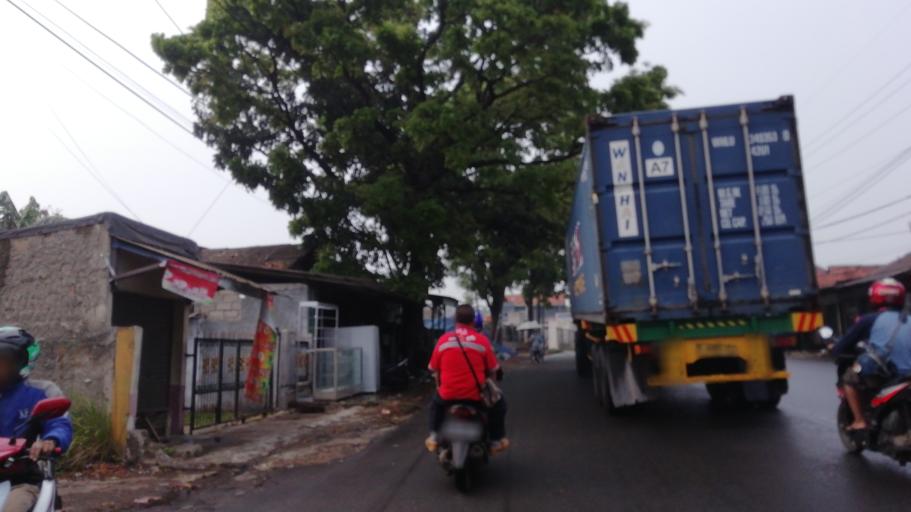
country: ID
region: West Java
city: Bogor
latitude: -6.5422
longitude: 106.8059
